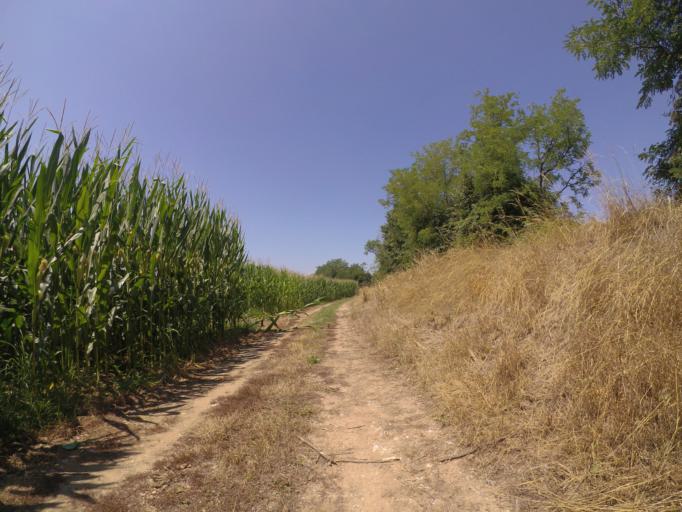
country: IT
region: Friuli Venezia Giulia
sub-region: Provincia di Udine
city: Varmo
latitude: 45.9258
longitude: 13.0122
